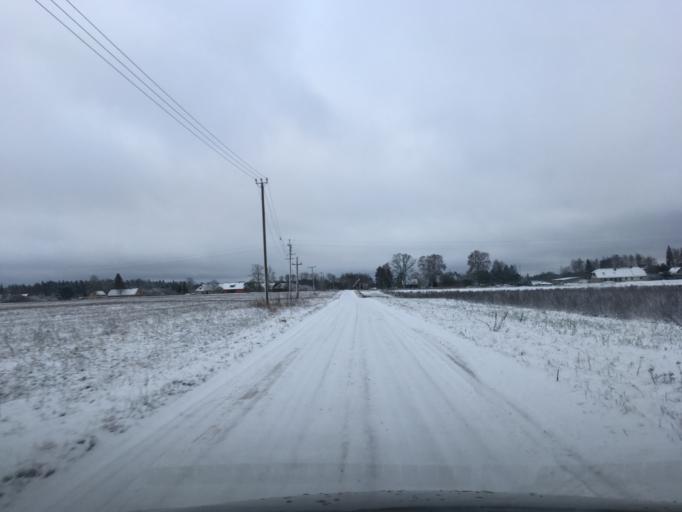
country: EE
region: Harju
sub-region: Raasiku vald
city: Raasiku
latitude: 59.2142
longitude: 25.1958
